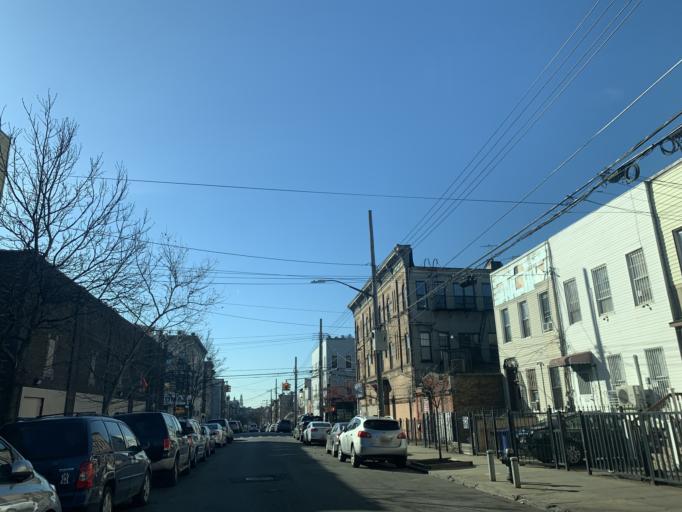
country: US
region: New York
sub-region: Kings County
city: East New York
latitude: 40.7021
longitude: -73.9143
